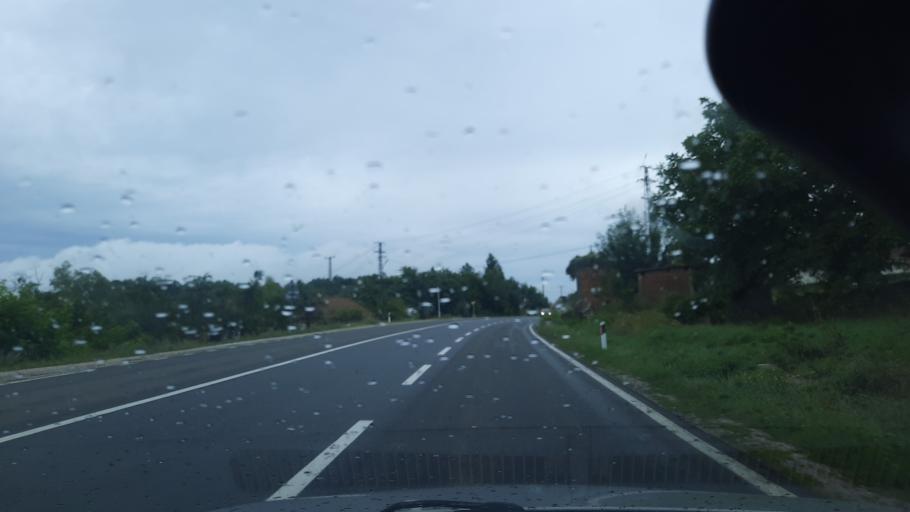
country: RS
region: Central Serbia
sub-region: Sumadijski Okrug
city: Knic
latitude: 43.9460
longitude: 20.7949
